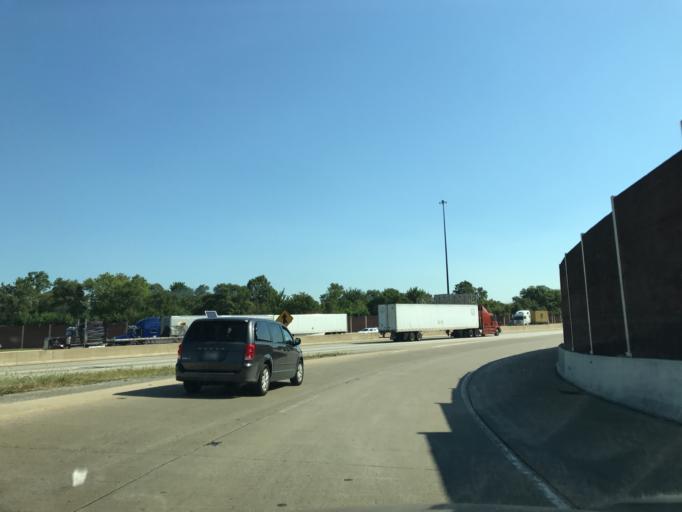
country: US
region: Indiana
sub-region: Lake County
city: Munster
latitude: 41.5735
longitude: -87.5073
